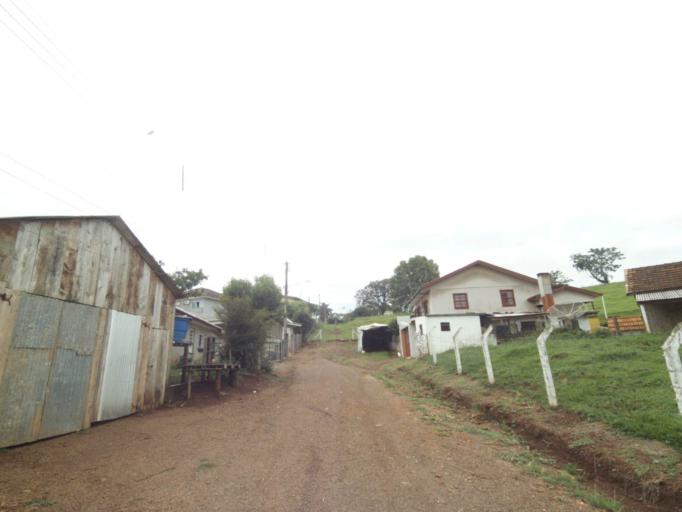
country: BR
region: Rio Grande do Sul
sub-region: Lagoa Vermelha
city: Lagoa Vermelha
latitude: -28.2180
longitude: -51.5359
